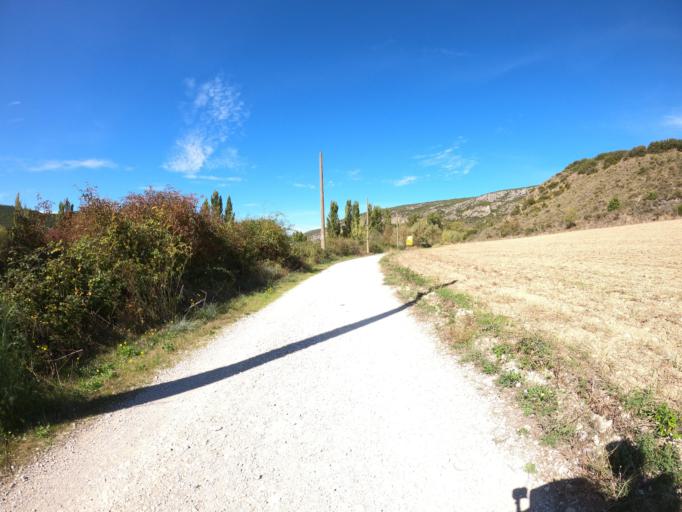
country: ES
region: Navarre
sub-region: Provincia de Navarra
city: Liedena
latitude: 42.6199
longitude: -1.2882
